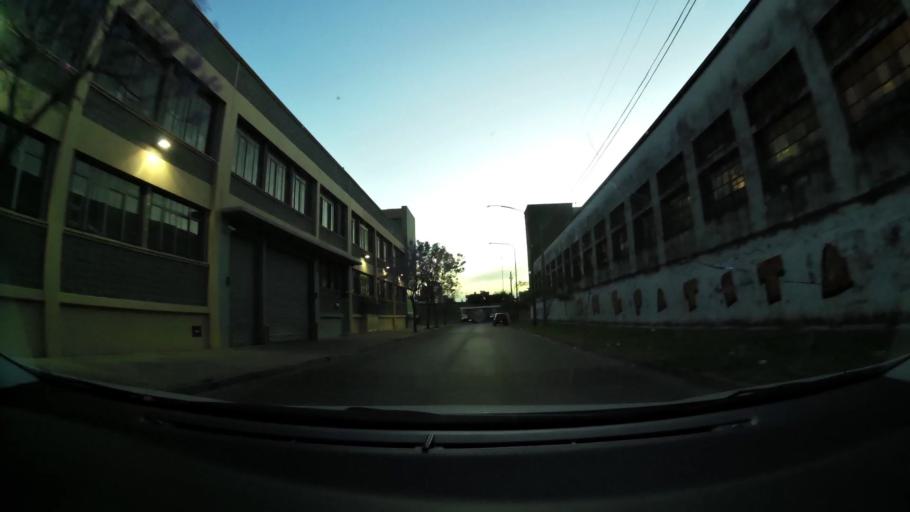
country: AR
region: Buenos Aires F.D.
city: Villa Lugano
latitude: -34.6968
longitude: -58.4703
